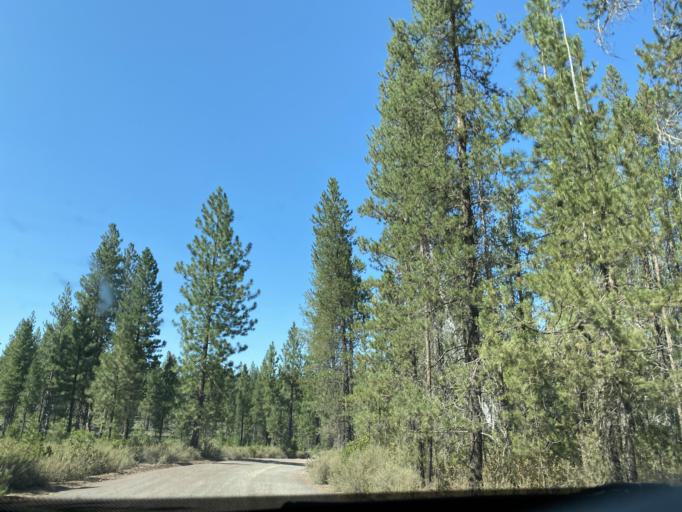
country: US
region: Oregon
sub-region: Deschutes County
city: Sunriver
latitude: 43.8777
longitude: -121.4667
